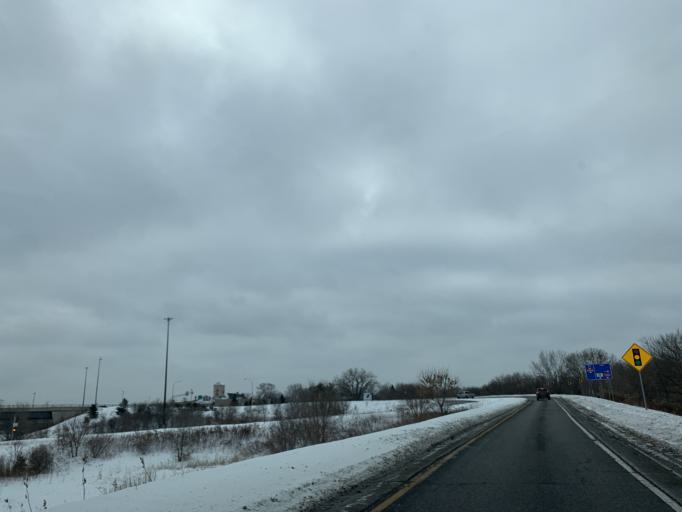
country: US
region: Minnesota
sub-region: Anoka County
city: Coon Rapids
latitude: 45.1531
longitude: -93.2767
